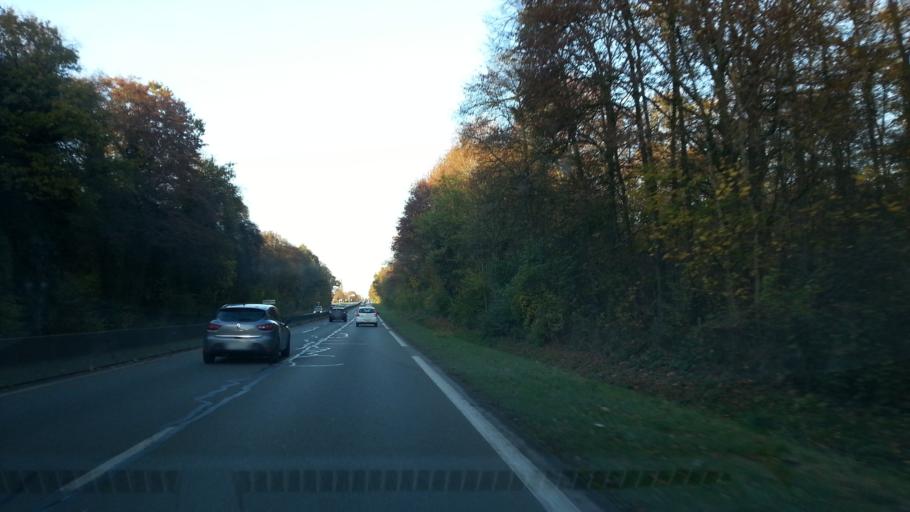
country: FR
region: Picardie
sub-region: Departement de l'Oise
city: Saint-Maximin
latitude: 49.2243
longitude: 2.4683
